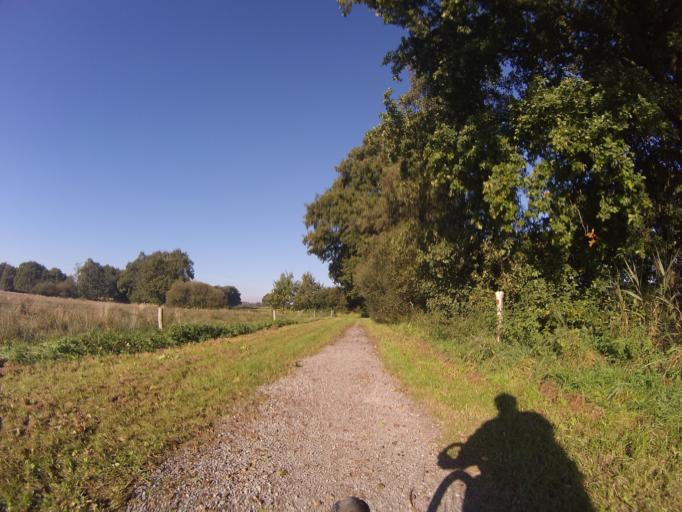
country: NL
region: Drenthe
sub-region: Gemeente Coevorden
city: Dalen
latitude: 52.7386
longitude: 6.6718
